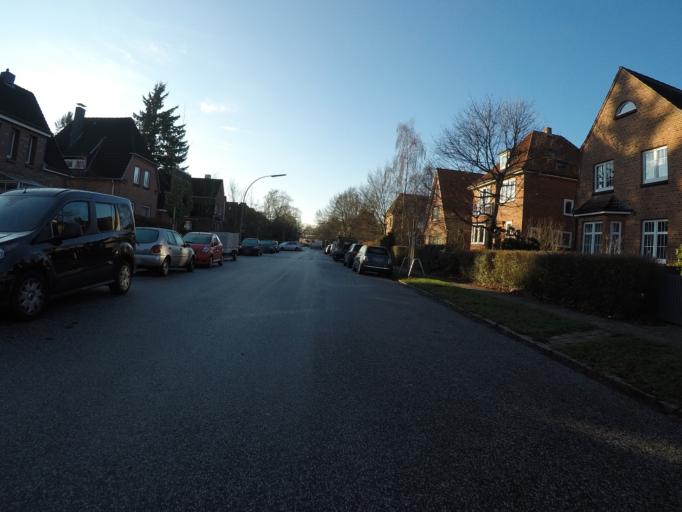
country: DE
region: Hamburg
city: Fuhlsbuettel
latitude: 53.6430
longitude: 10.0222
